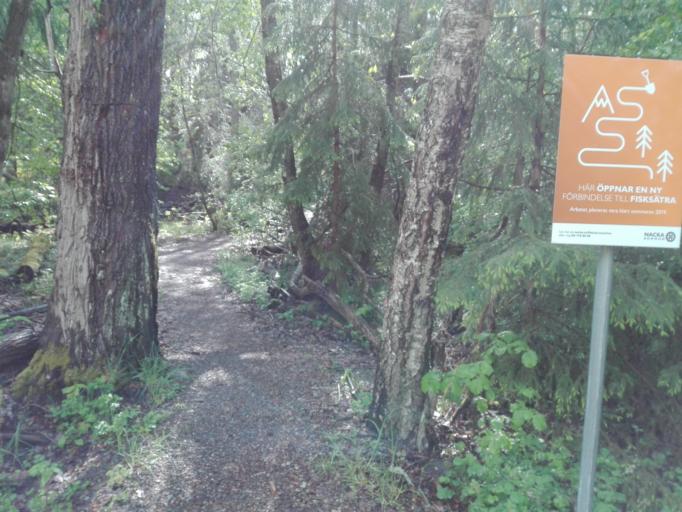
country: SE
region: Stockholm
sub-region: Nacka Kommun
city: Fisksatra
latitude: 59.2951
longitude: 18.2769
